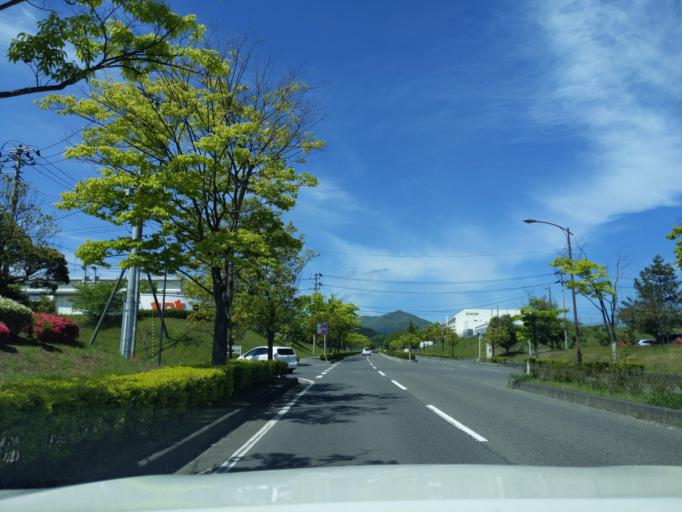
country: JP
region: Fukushima
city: Koriyama
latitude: 37.4471
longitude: 140.3023
